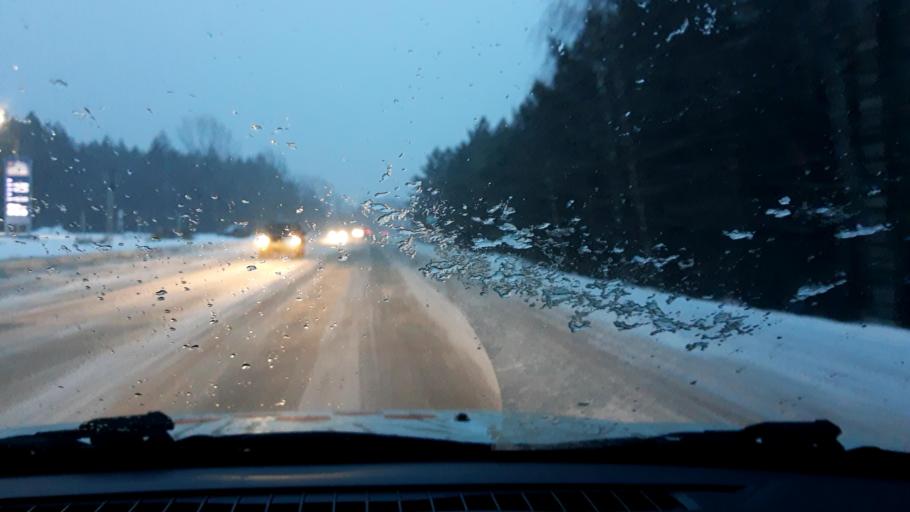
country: RU
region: Nizjnij Novgorod
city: Bor
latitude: 56.3250
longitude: 44.1405
